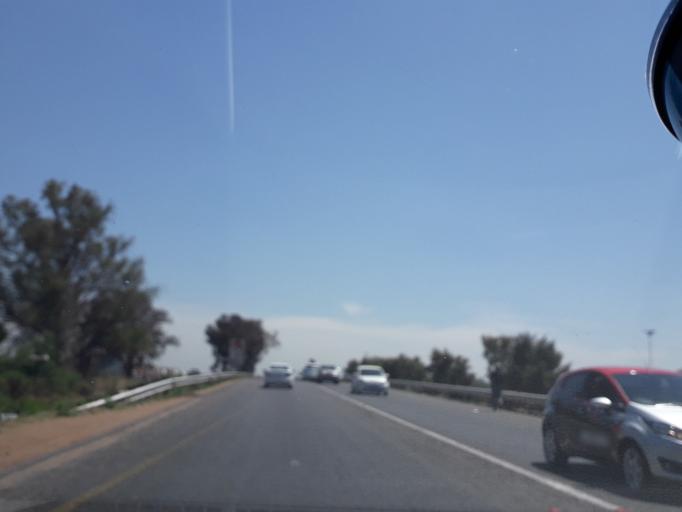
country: ZA
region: Gauteng
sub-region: City of Tshwane Metropolitan Municipality
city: Centurion
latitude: -25.8834
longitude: 28.1613
